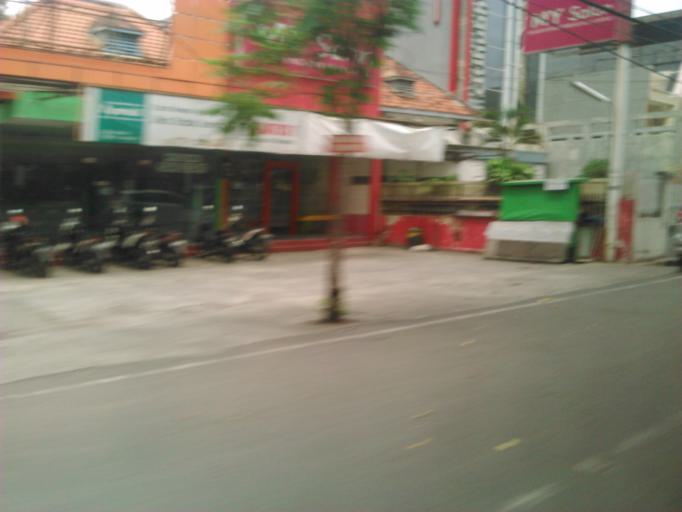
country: ID
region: East Java
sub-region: Kota Surabaya
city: Surabaya
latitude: -7.2621
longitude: 112.7267
